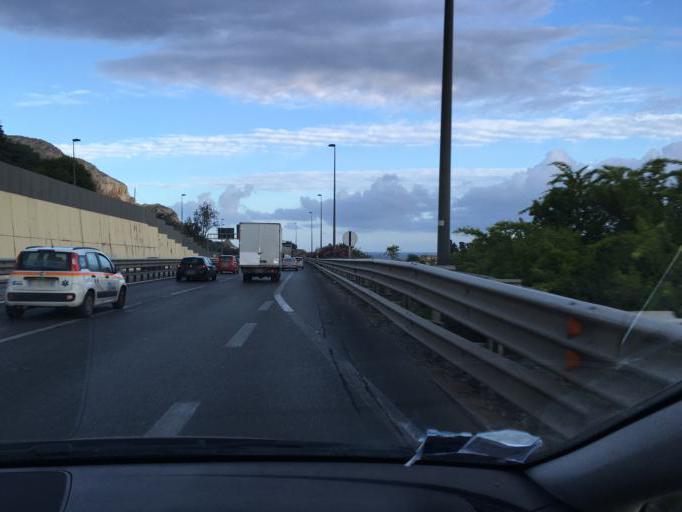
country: IT
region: Sicily
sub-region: Palermo
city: Isola delle Femmine
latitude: 38.1929
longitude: 13.2801
